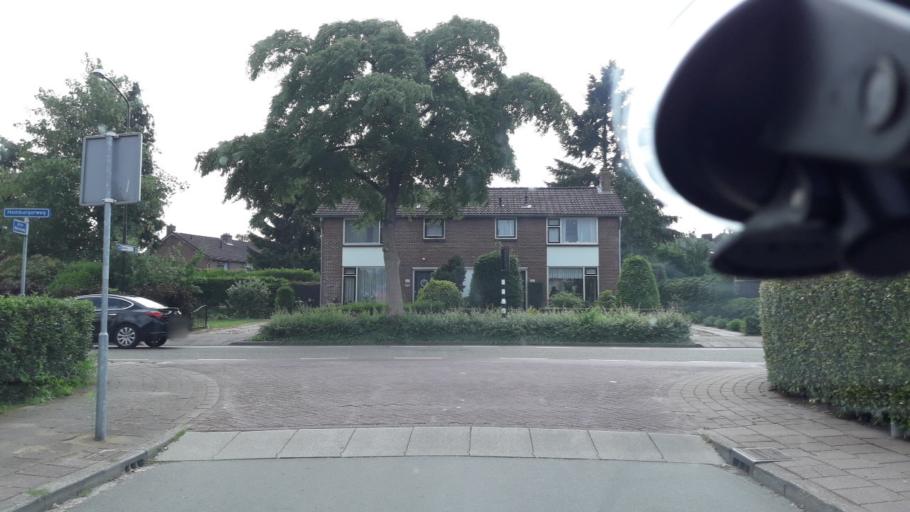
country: NL
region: Gelderland
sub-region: Gemeente Ermelo
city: Ermelo
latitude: 52.2963
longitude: 5.6167
